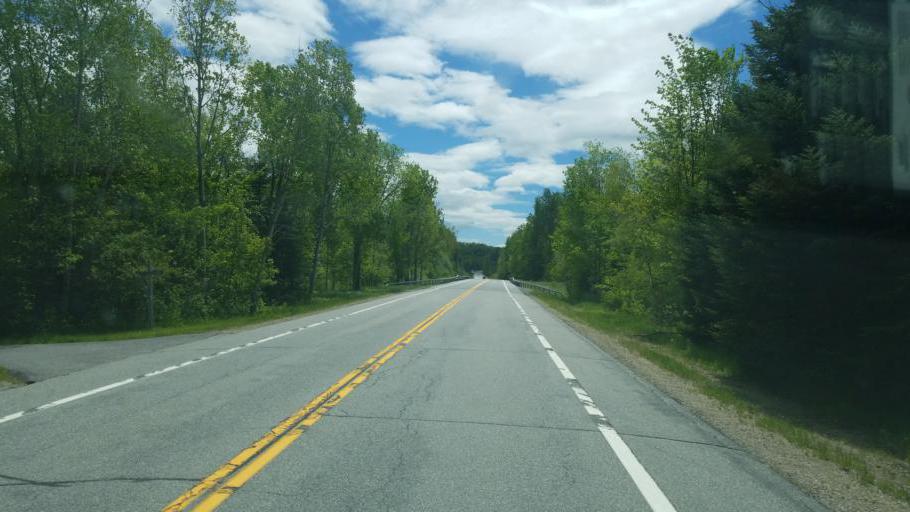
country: US
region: New York
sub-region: Hamilton County
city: Lake Pleasant
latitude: 43.7089
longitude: -74.3315
